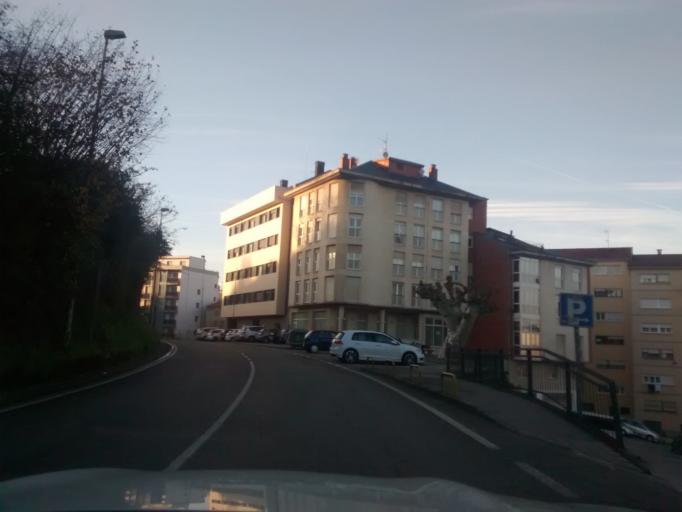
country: ES
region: Cantabria
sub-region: Provincia de Cantabria
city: Lierganes
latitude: 43.3840
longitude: -3.7332
